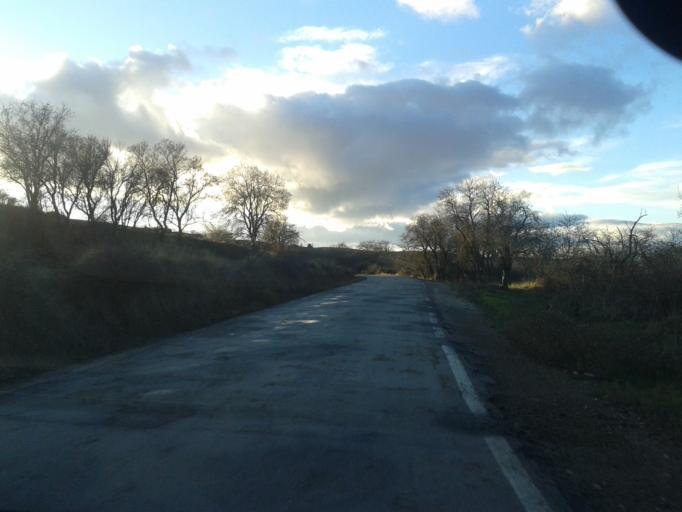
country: ES
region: Aragon
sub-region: Provincia de Teruel
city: Lagueruela
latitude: 41.0401
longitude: -1.1965
